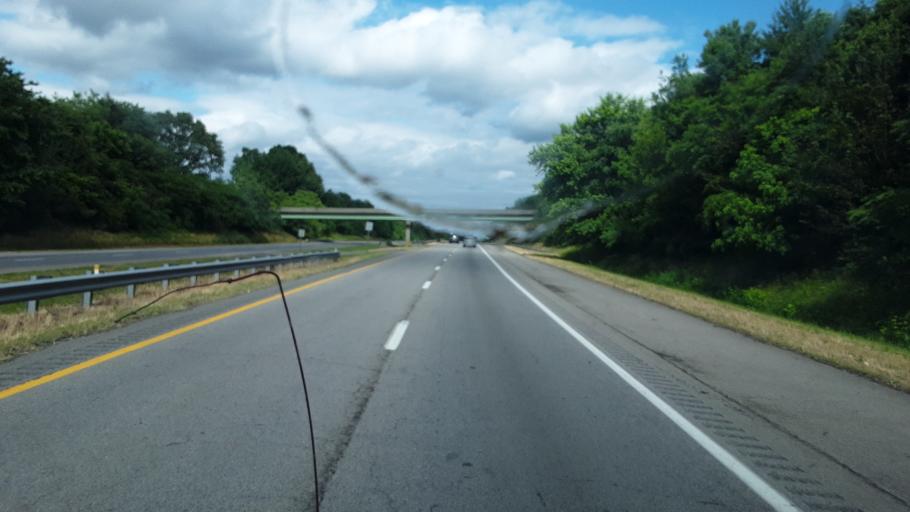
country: US
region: Virginia
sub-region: City of Danville
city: Danville
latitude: 36.5463
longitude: -79.4341
